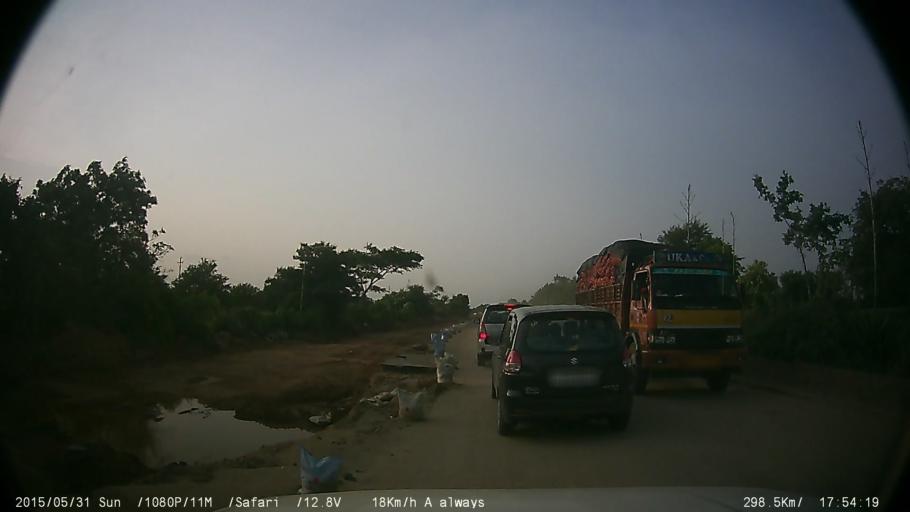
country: IN
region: Karnataka
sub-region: Mysore
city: Nanjangud
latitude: 11.9869
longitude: 76.6695
